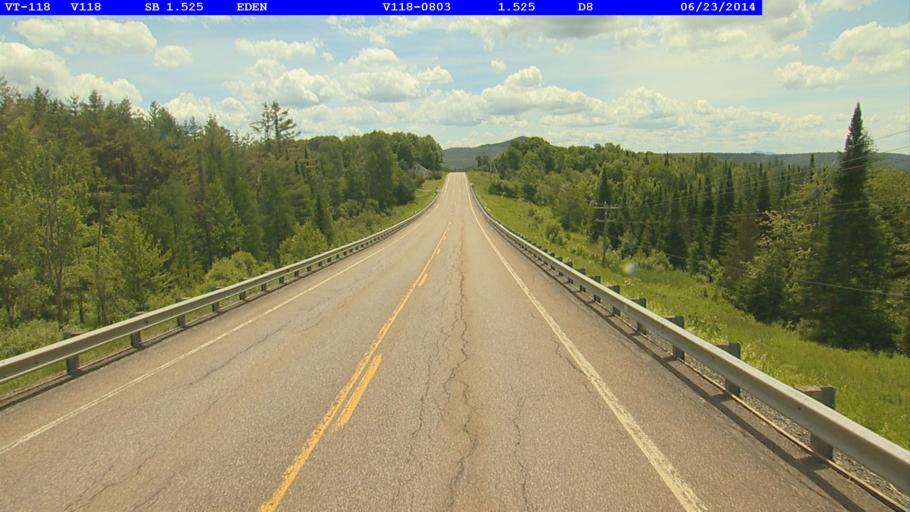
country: US
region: Vermont
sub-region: Lamoille County
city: Hyde Park
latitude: 44.7261
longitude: -72.5614
